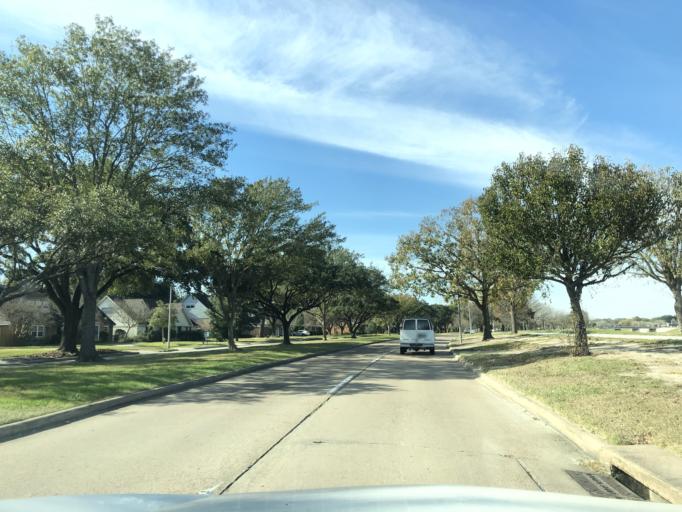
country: US
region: Texas
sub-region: Harris County
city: Bellaire
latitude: 29.6748
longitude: -95.4871
